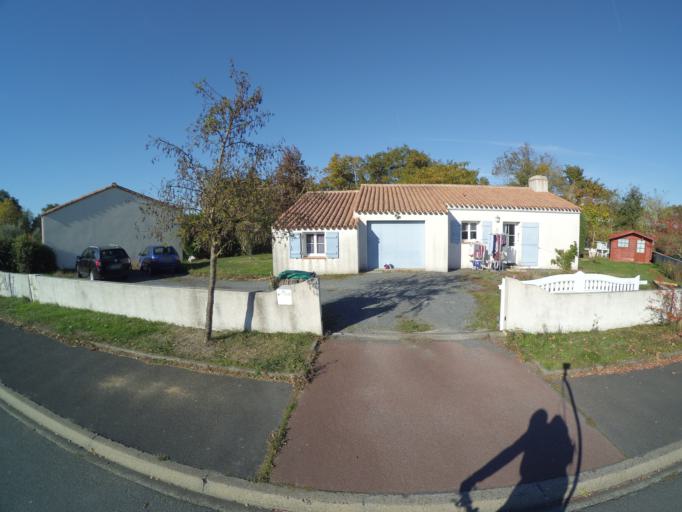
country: FR
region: Pays de la Loire
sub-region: Departement de la Loire-Atlantique
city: Saint-Lumine-de-Clisson
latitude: 47.0875
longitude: -1.3320
